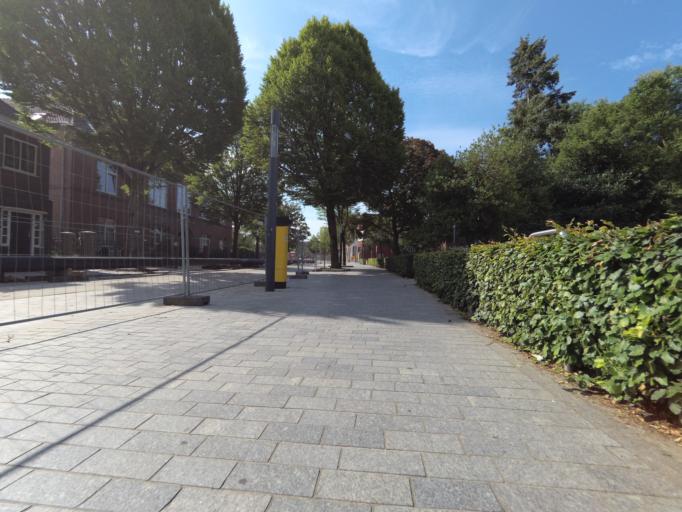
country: NL
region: Overijssel
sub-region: Gemeente Enschede
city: Enschede
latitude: 52.2251
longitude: 6.8948
